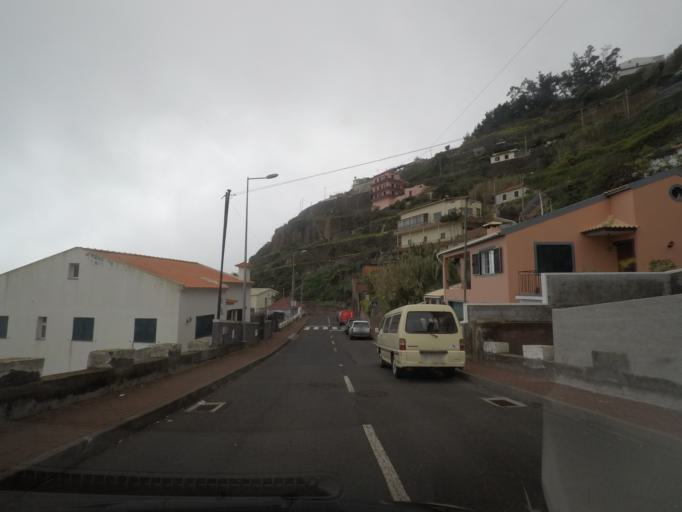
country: PT
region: Madeira
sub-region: Ribeira Brava
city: Campanario
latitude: 32.6622
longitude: -17.0126
